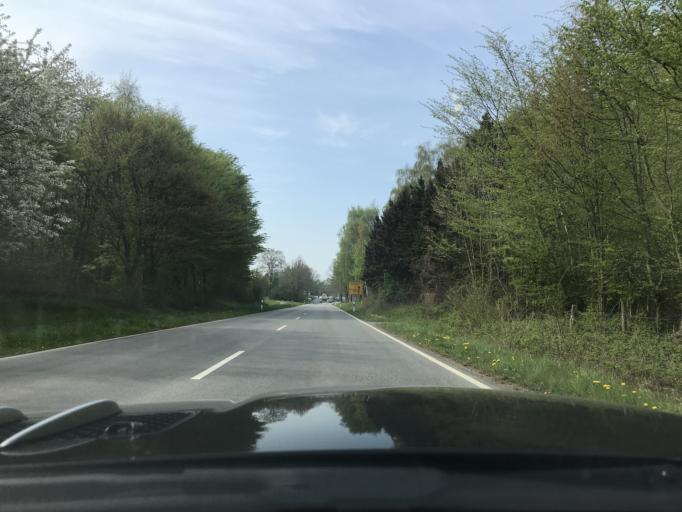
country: DE
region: Schleswig-Holstein
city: Grube
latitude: 54.2002
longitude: 11.0281
